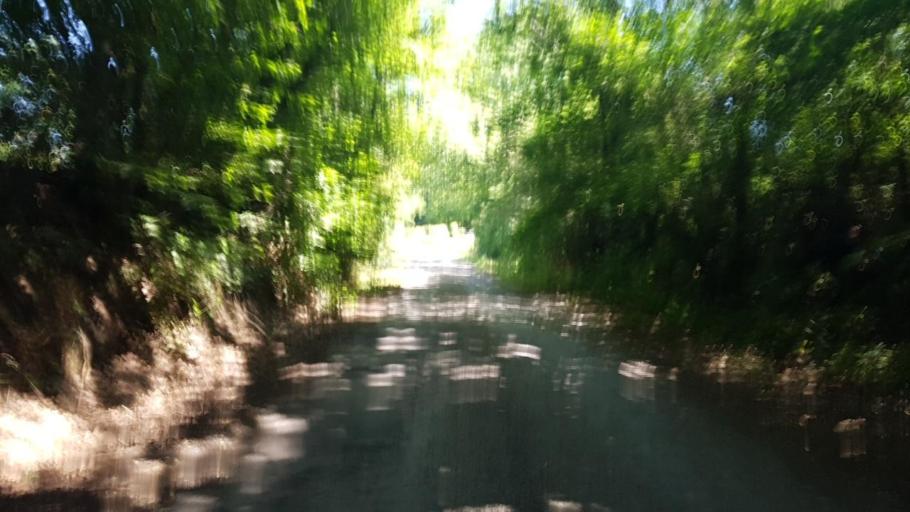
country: BE
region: Wallonia
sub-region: Province du Hainaut
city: Momignies
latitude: 50.0952
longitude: 4.2274
